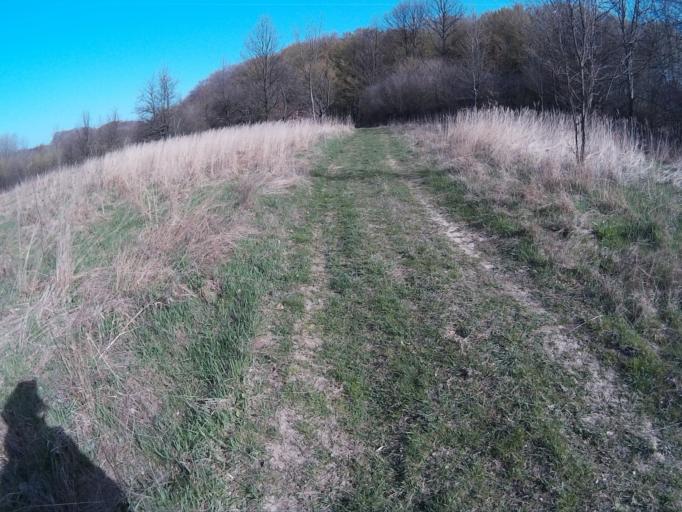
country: HU
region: Veszprem
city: Herend
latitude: 47.2035
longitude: 17.7894
